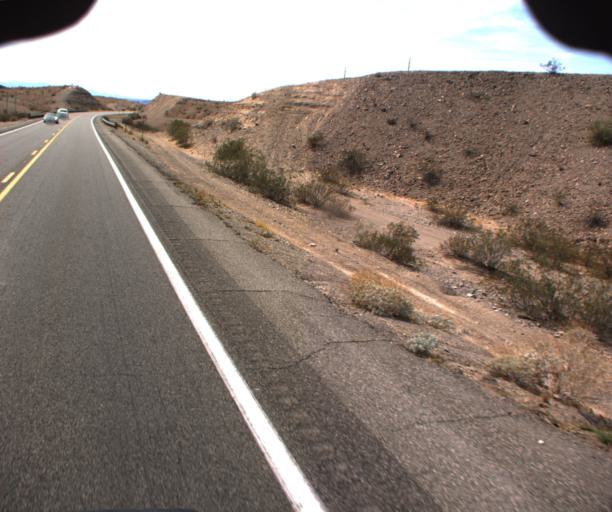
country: US
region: Arizona
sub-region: Mohave County
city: Lake Havasu City
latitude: 34.4511
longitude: -114.2573
